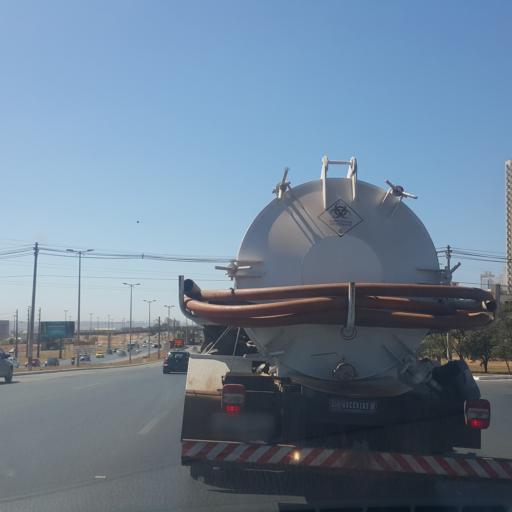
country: BR
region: Federal District
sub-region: Brasilia
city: Brasilia
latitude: -15.8320
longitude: -48.0495
